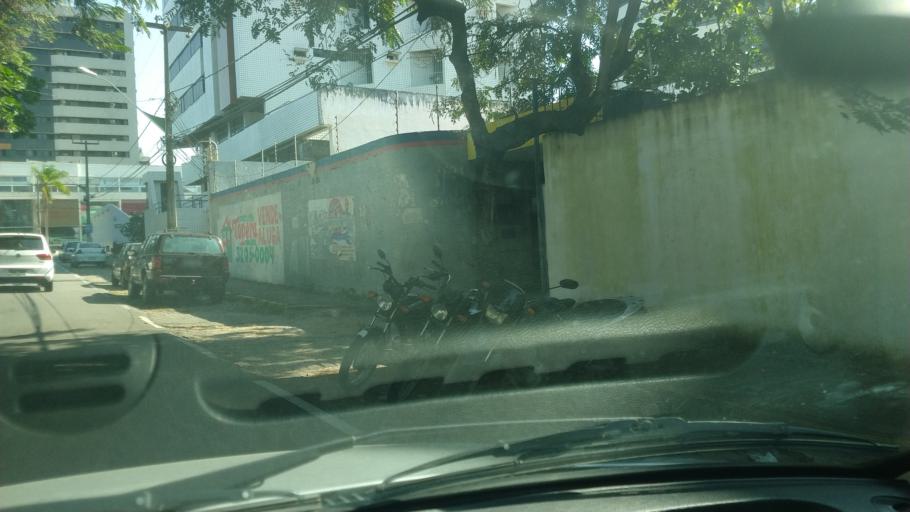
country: BR
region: Rio Grande do Norte
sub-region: Natal
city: Natal
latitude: -5.8001
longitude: -35.2017
